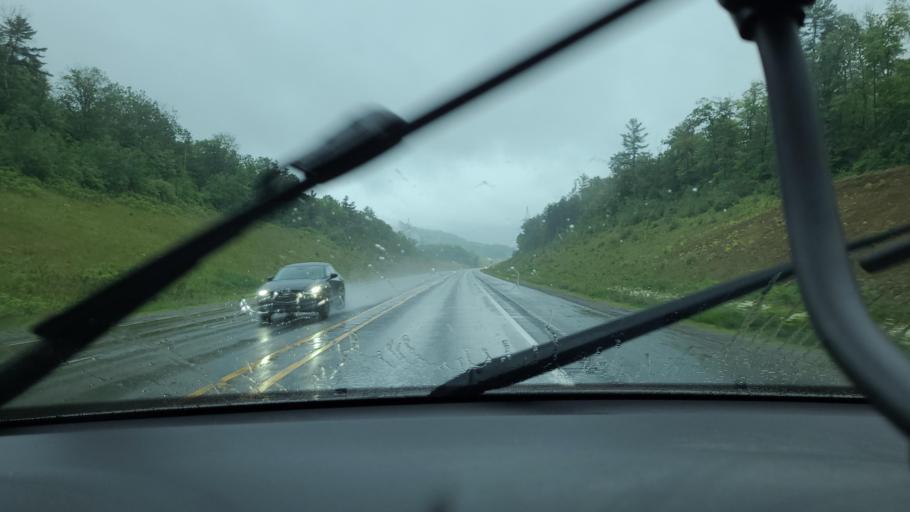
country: CA
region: Quebec
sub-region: Outaouais
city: Papineauville
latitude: 45.6655
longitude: -74.8922
